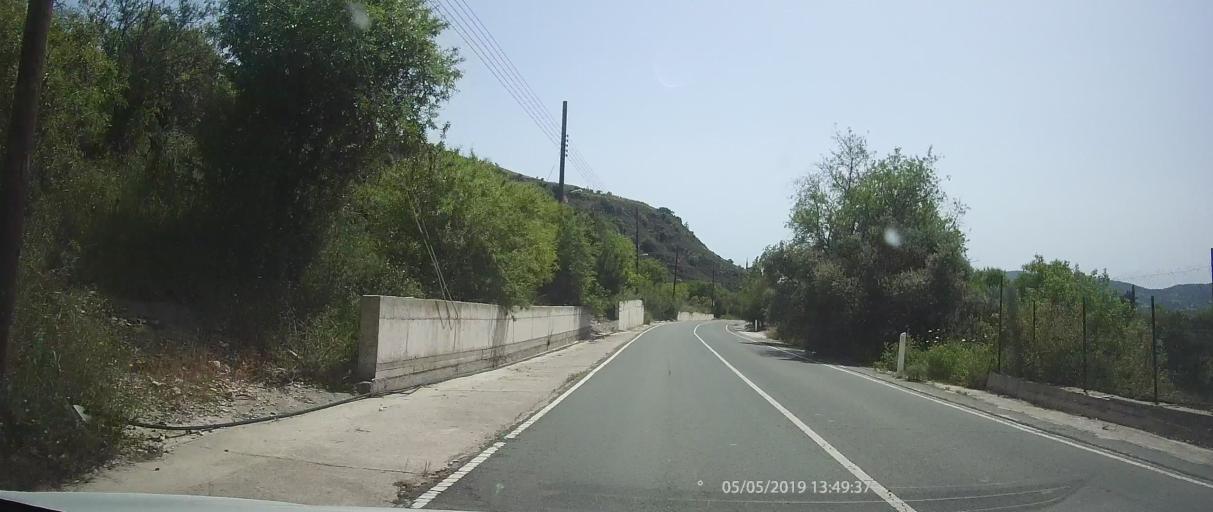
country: CY
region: Limassol
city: Pachna
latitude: 34.8477
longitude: 32.7476
